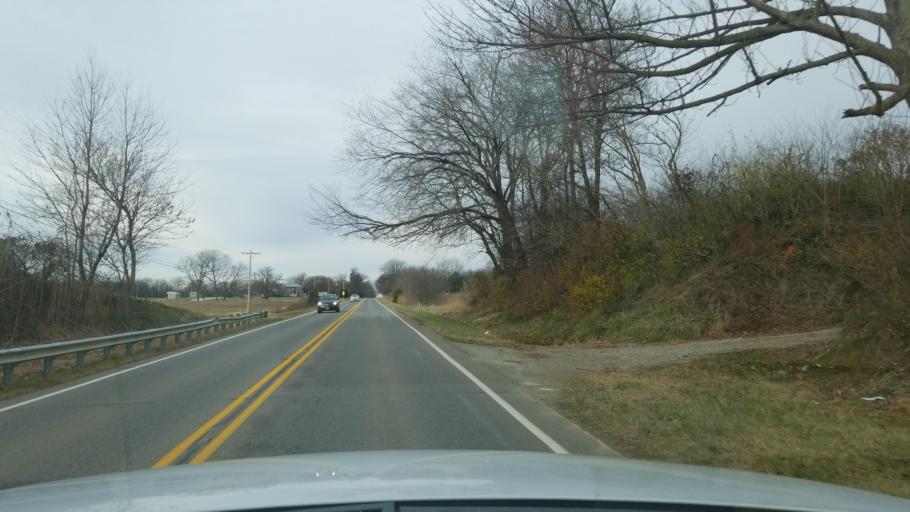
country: US
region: Indiana
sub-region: Posey County
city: Mount Vernon
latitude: 37.9291
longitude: -87.9462
